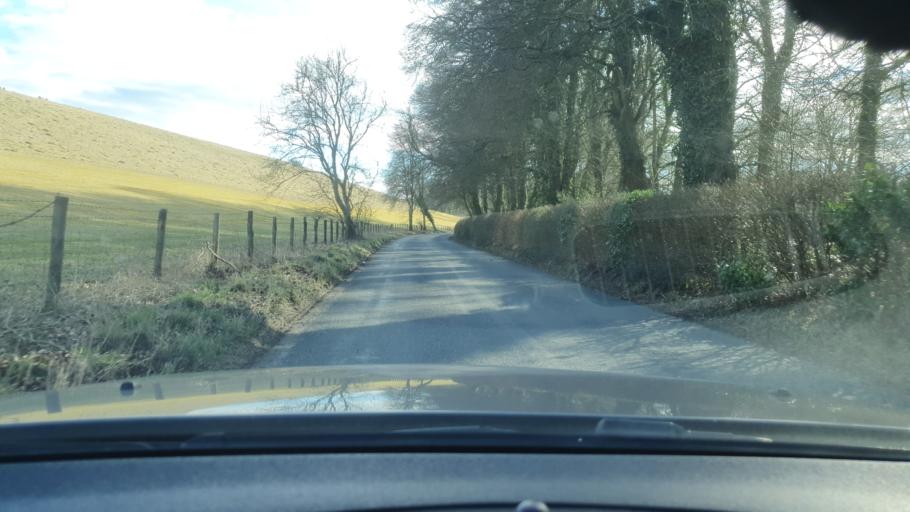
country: GB
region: England
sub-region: Wiltshire
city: Fyfield
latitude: 51.4484
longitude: -1.7624
